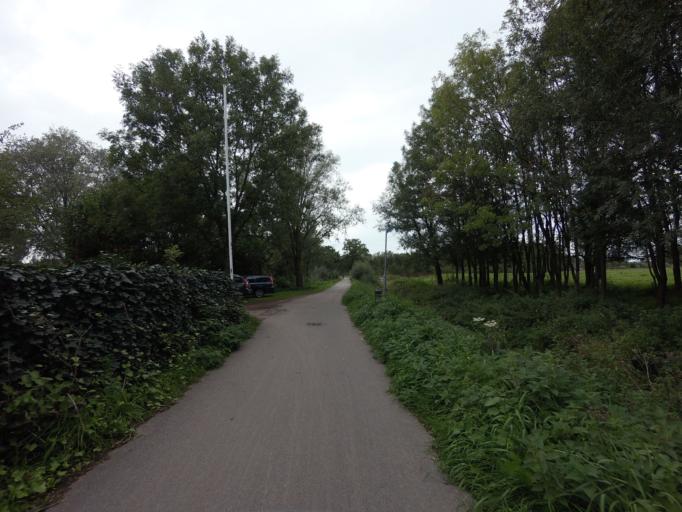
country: NL
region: Friesland
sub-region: Gemeente Leeuwarden
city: Bilgaard
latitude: 53.2197
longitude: 5.7929
